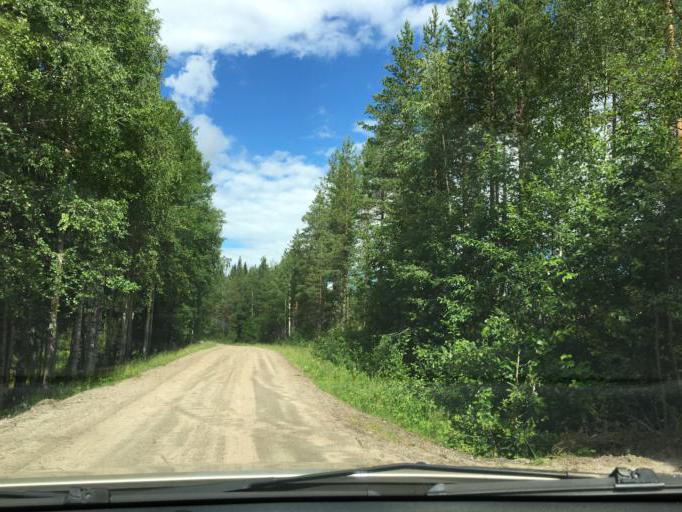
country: SE
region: Norrbotten
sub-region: Overkalix Kommun
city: OEverkalix
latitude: 66.1307
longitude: 22.7847
